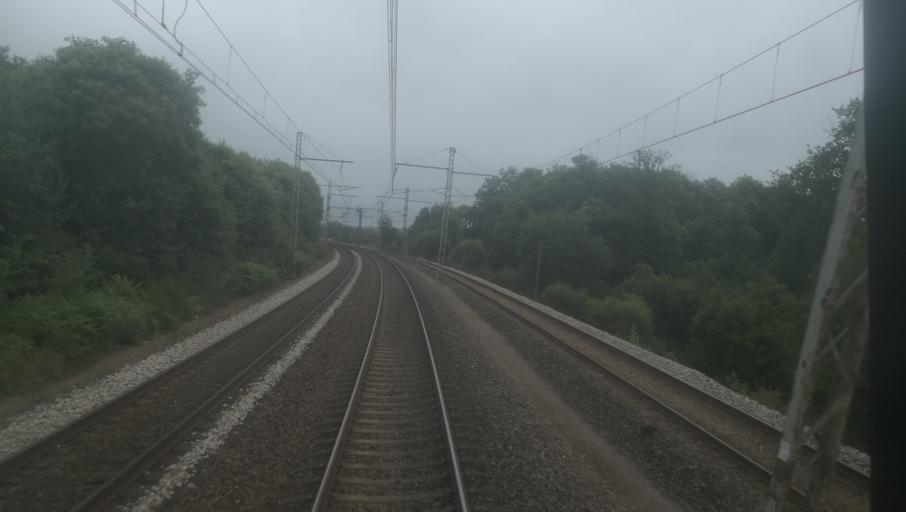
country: FR
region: Limousin
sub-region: Departement de la Creuse
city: Saint-Agnant-de-Versillat
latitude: 46.3164
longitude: 1.5223
